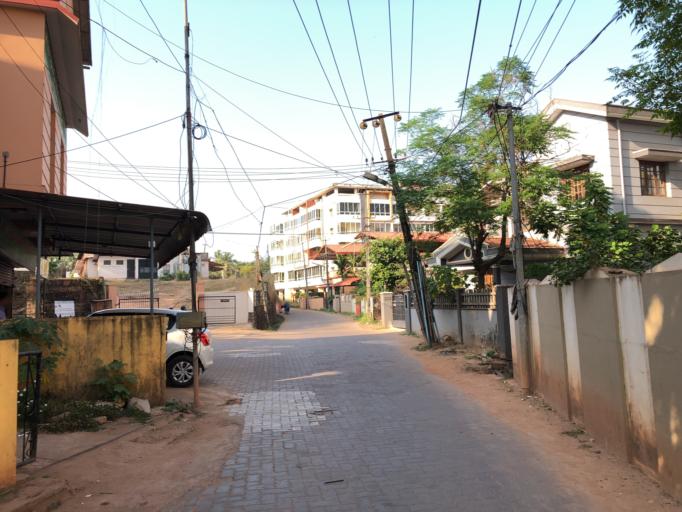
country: IN
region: Karnataka
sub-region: Dakshina Kannada
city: Mangalore
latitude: 12.8705
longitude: 74.8745
